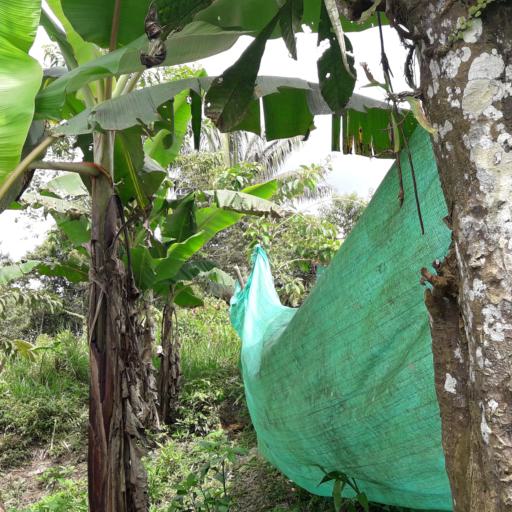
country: EC
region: Napo
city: Archidona
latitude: -0.9416
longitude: -77.8747
